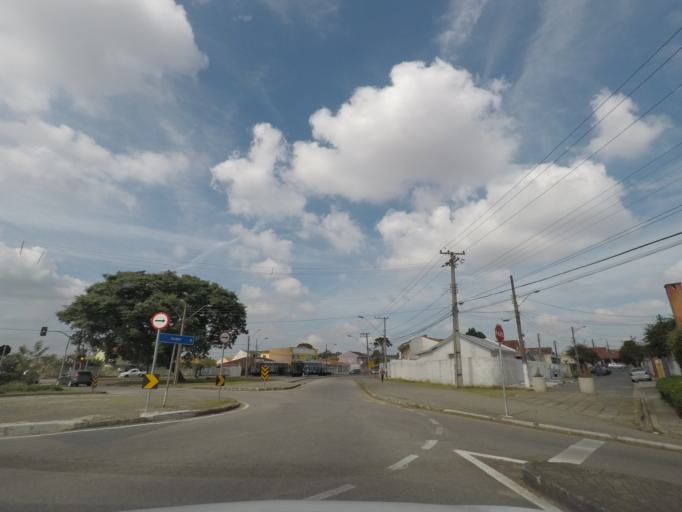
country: BR
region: Parana
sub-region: Pinhais
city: Pinhais
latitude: -25.4467
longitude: -49.2176
